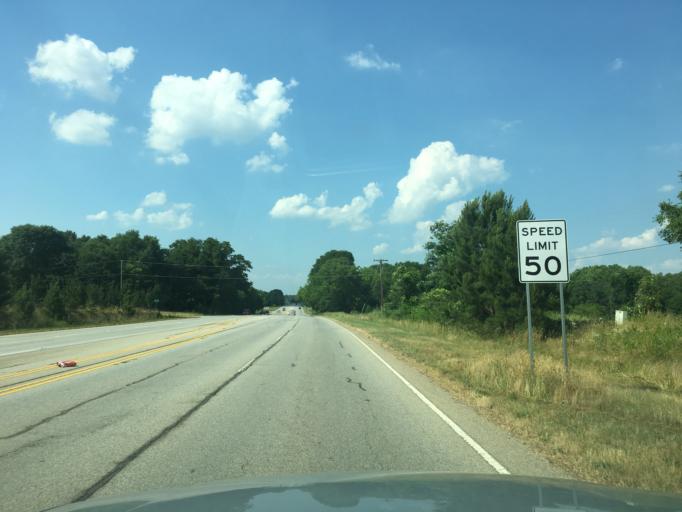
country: US
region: South Carolina
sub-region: Anderson County
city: Northlake
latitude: 34.6053
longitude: -82.6117
